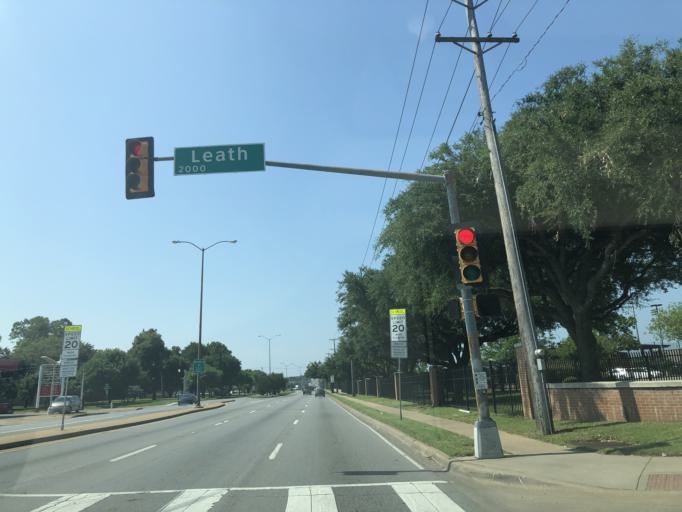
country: US
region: Texas
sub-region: Dallas County
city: Dallas
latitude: 32.7895
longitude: -96.8566
